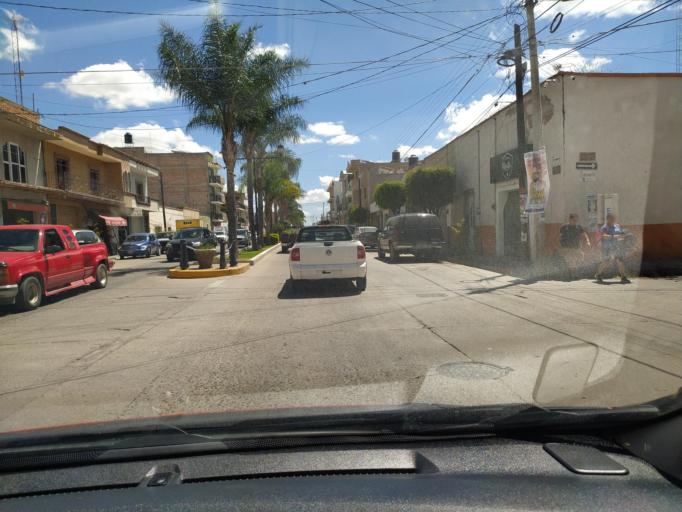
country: MX
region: Jalisco
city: San Julian
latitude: 21.0103
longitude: -102.1782
